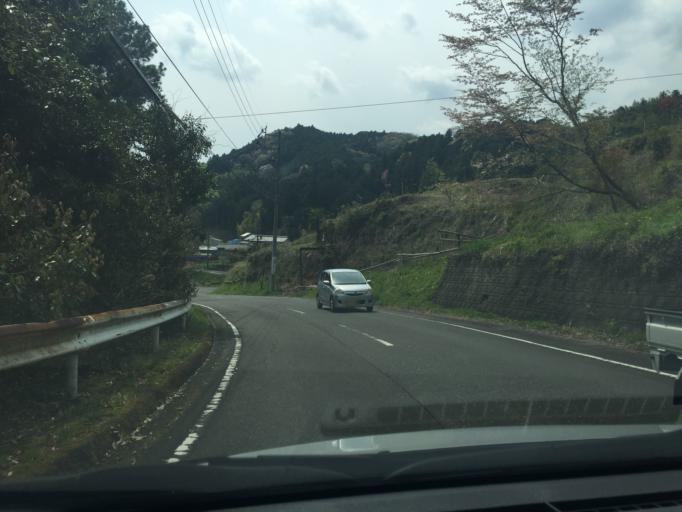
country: JP
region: Shizuoka
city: Kakegawa
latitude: 34.8378
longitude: 138.0455
